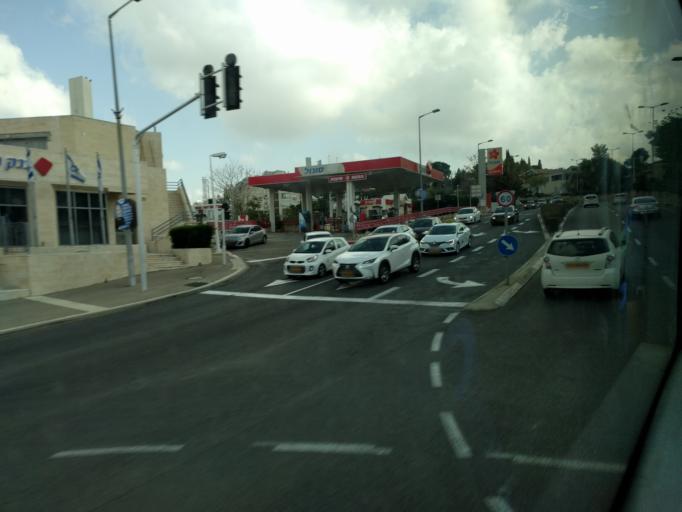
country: IL
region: Haifa
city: Tirat Karmel
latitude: 32.7695
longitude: 35.0070
